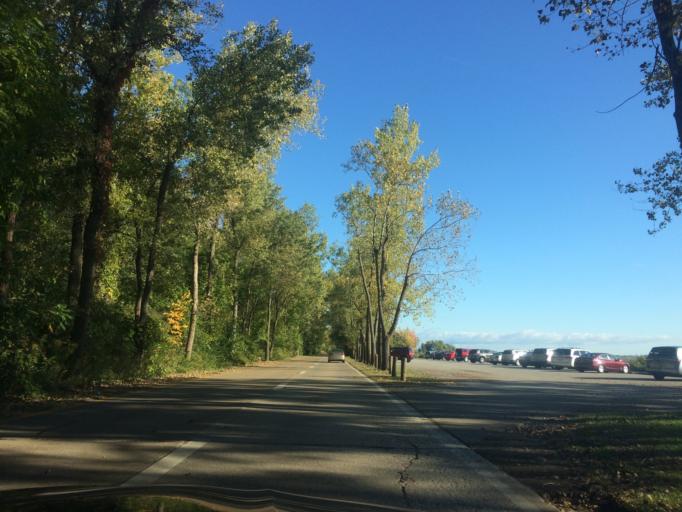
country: US
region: Pennsylvania
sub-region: Erie County
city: Erie
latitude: 42.1190
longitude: -80.1498
